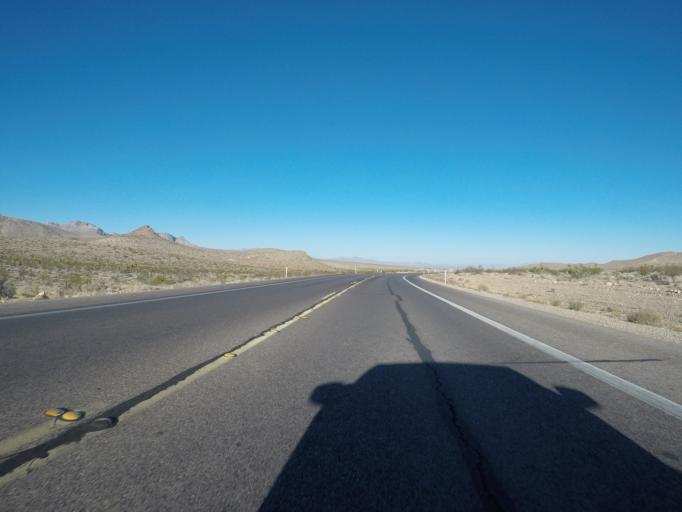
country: US
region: Nevada
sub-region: Clark County
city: Summerlin South
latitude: 36.1398
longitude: -115.4034
